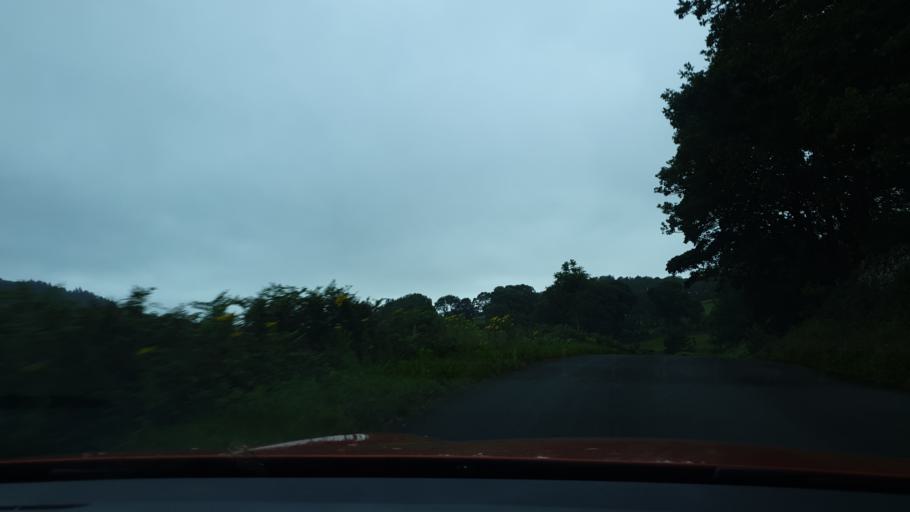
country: GB
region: England
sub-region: Cumbria
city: Seascale
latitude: 54.4168
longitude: -3.3549
